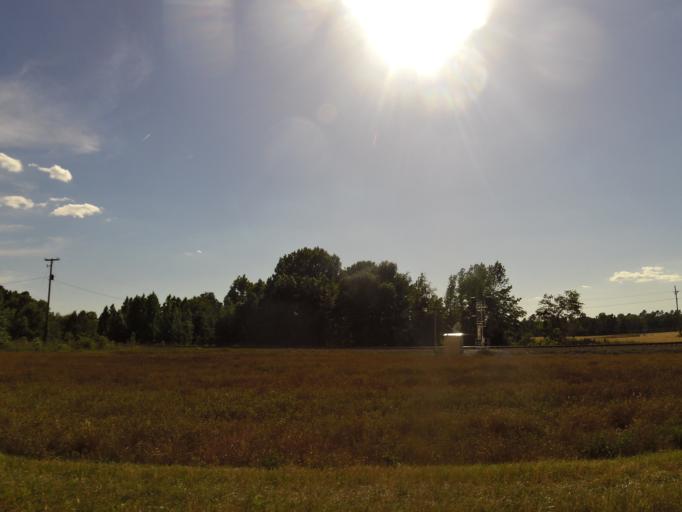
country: US
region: South Carolina
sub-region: Allendale County
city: Fairfax
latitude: 33.0299
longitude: -81.2230
